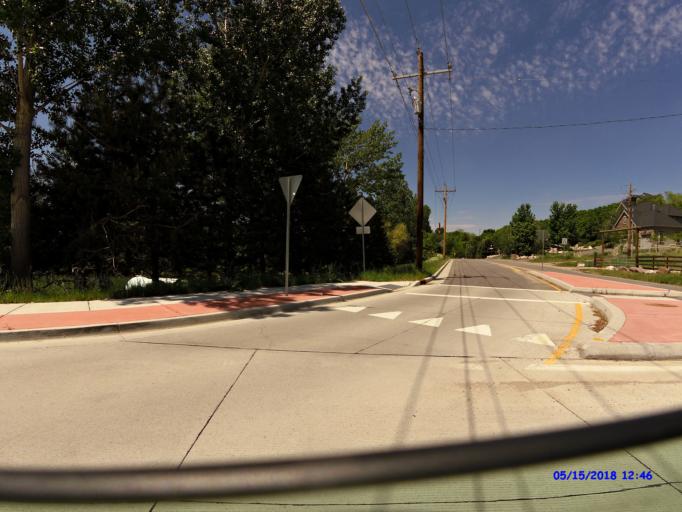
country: US
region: Utah
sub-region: Weber County
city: Uintah
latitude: 41.1595
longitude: -111.9271
